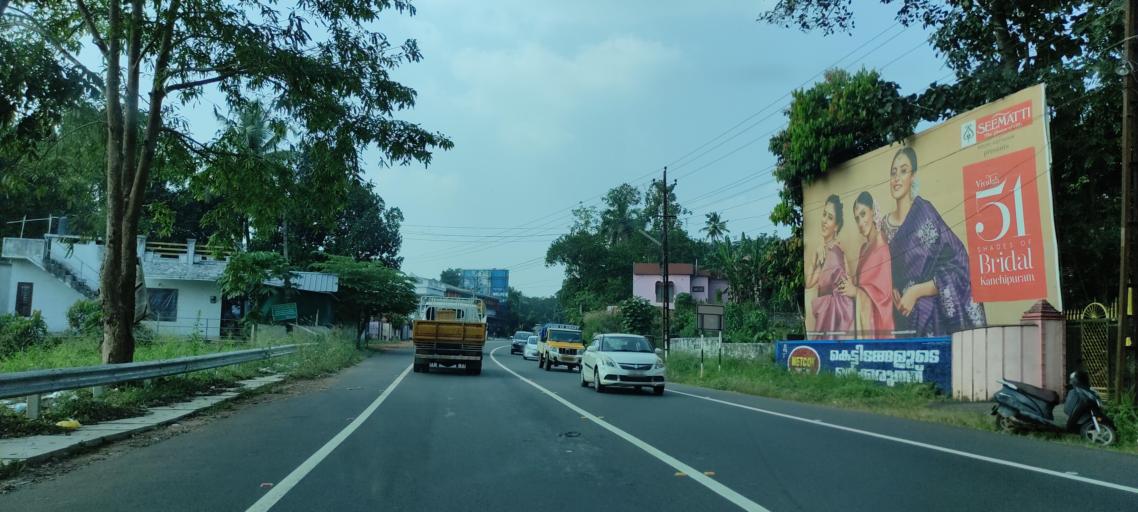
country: IN
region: Kerala
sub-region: Alappuzha
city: Chengannur
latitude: 9.2587
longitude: 76.6589
